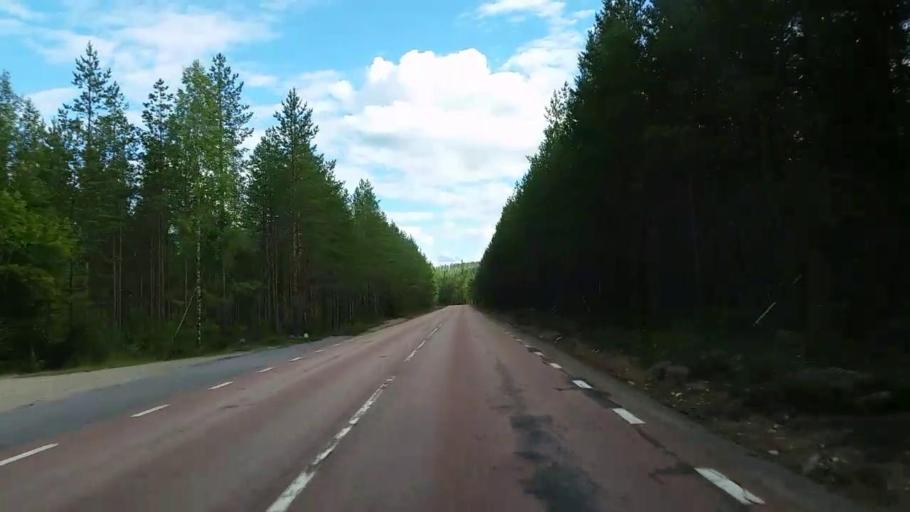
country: SE
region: Gaevleborg
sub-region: Ljusdals Kommun
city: Farila
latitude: 61.9813
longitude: 15.8573
